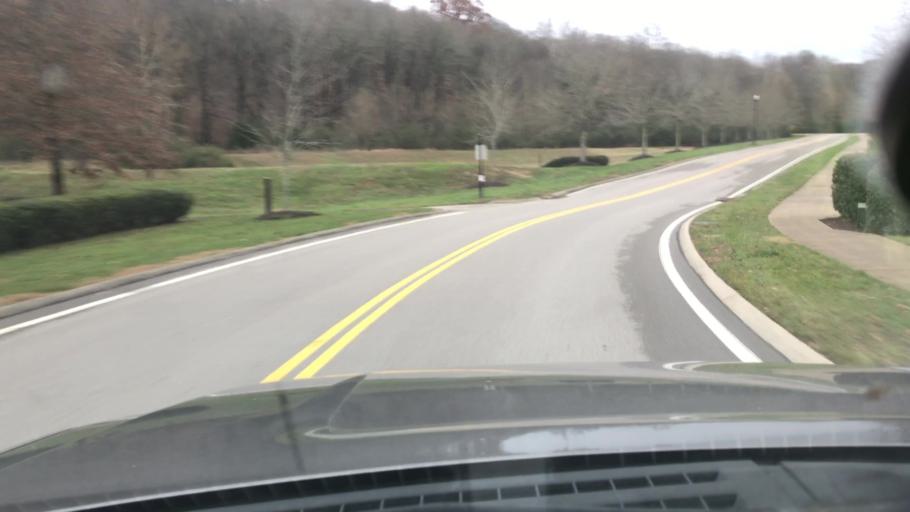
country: US
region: Tennessee
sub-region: Williamson County
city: Brentwood Estates
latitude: 35.9723
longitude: -86.7392
